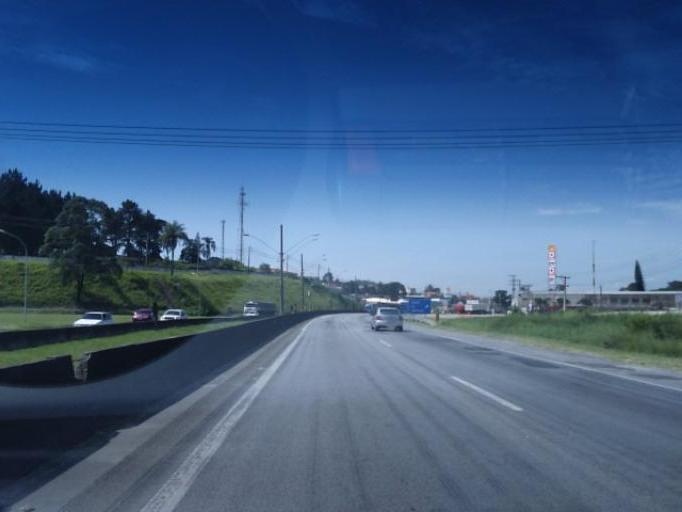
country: BR
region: Sao Paulo
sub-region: Itapecerica Da Serra
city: Itapecerica da Serra
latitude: -23.6836
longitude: -46.8592
